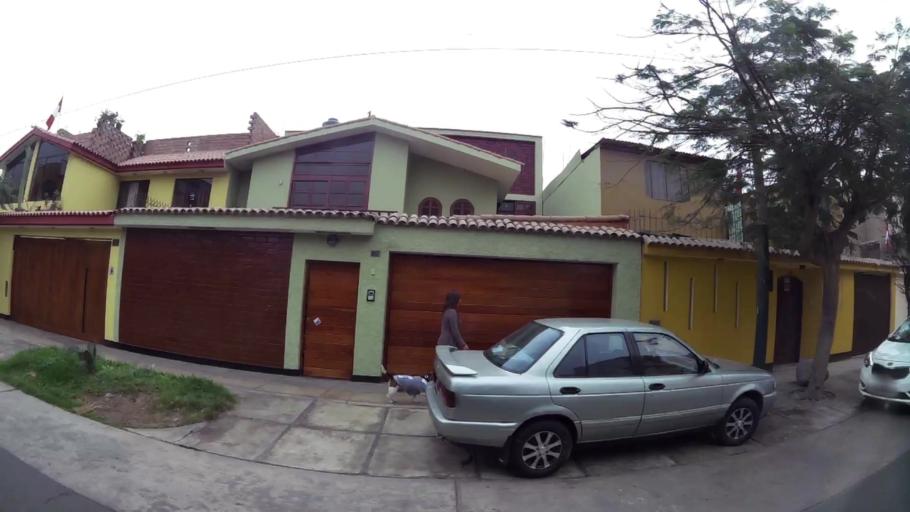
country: PE
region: Lima
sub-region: Lima
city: Surco
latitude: -12.1400
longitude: -76.9958
